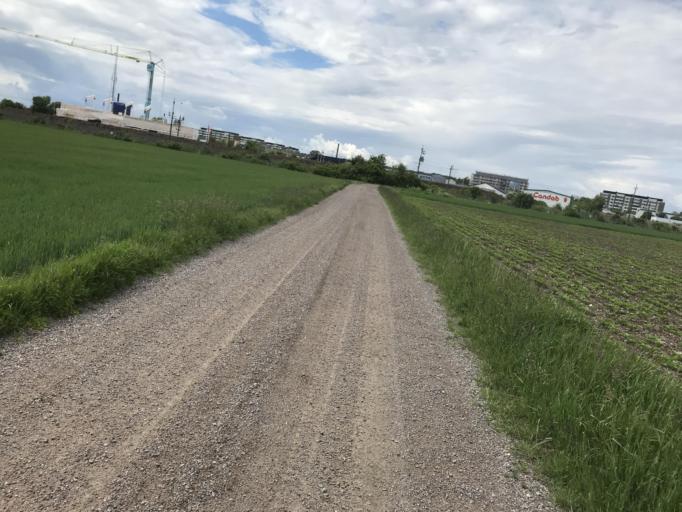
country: SE
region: Skane
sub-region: Landskrona
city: Landskrona
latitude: 55.8877
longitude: 12.8578
